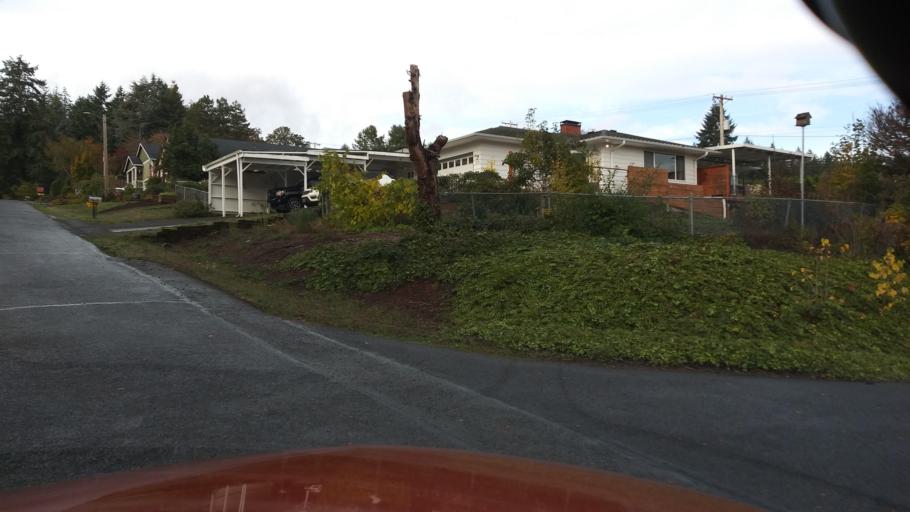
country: US
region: Oregon
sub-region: Washington County
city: Forest Grove
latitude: 45.5326
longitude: -123.1350
